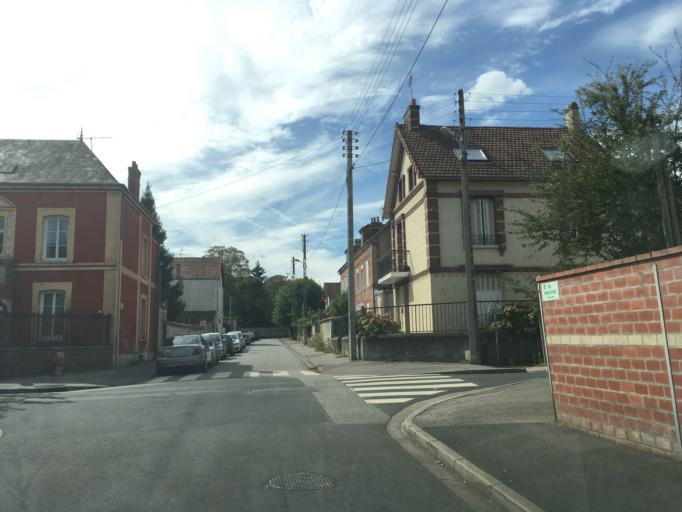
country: FR
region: Haute-Normandie
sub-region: Departement de l'Eure
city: Vernon
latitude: 49.0965
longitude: 1.4788
